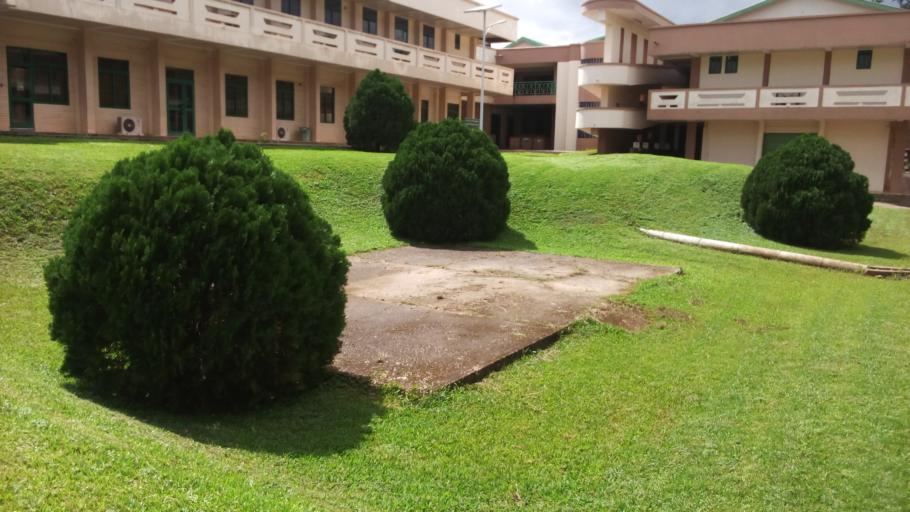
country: GH
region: Western
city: Tarkwa
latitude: 5.2988
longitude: -2.0000
